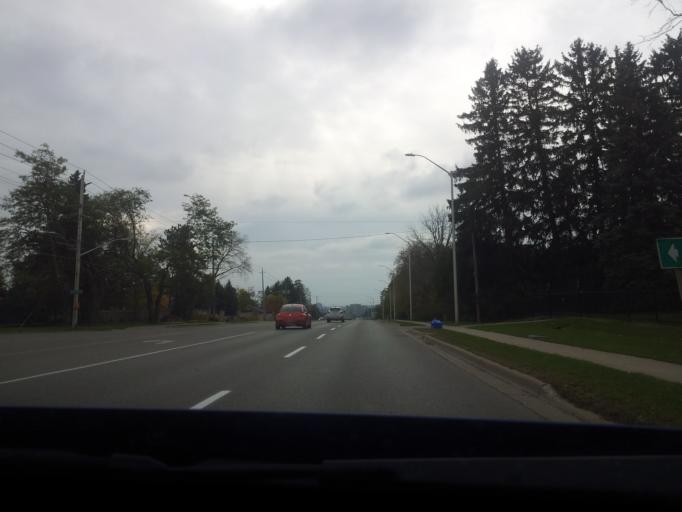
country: CA
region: Ontario
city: London
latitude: 43.0345
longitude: -81.2869
